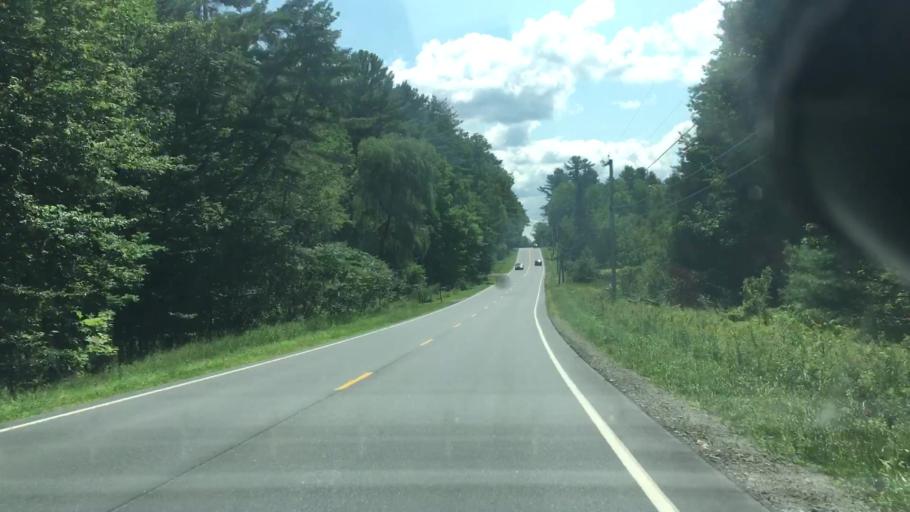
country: US
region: Maine
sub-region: Somerset County
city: Skowhegan
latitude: 44.6663
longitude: -69.6810
